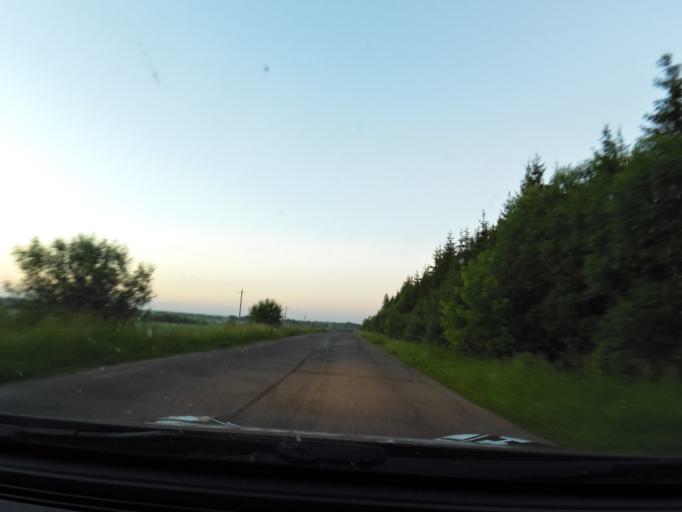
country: RU
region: Kostroma
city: Buy
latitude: 58.4567
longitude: 41.3807
